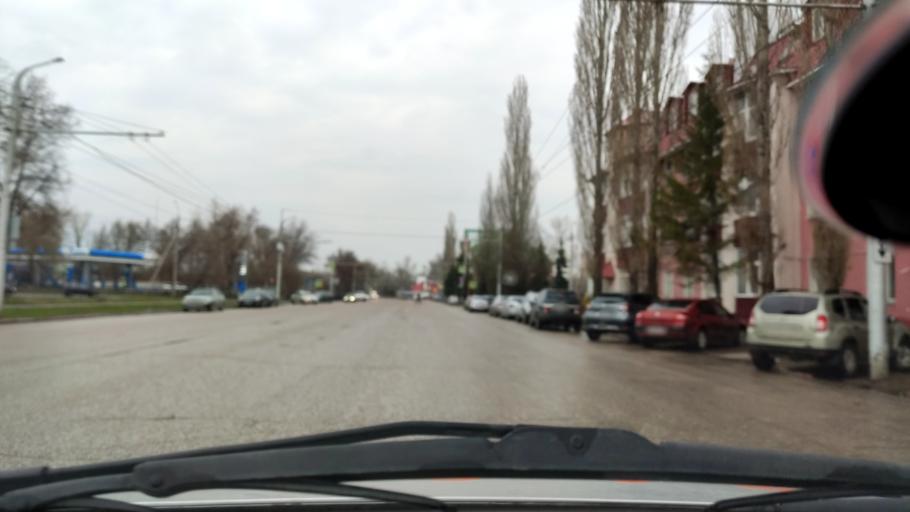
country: RU
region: Bashkortostan
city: Sterlitamak
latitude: 53.6521
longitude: 55.9471
